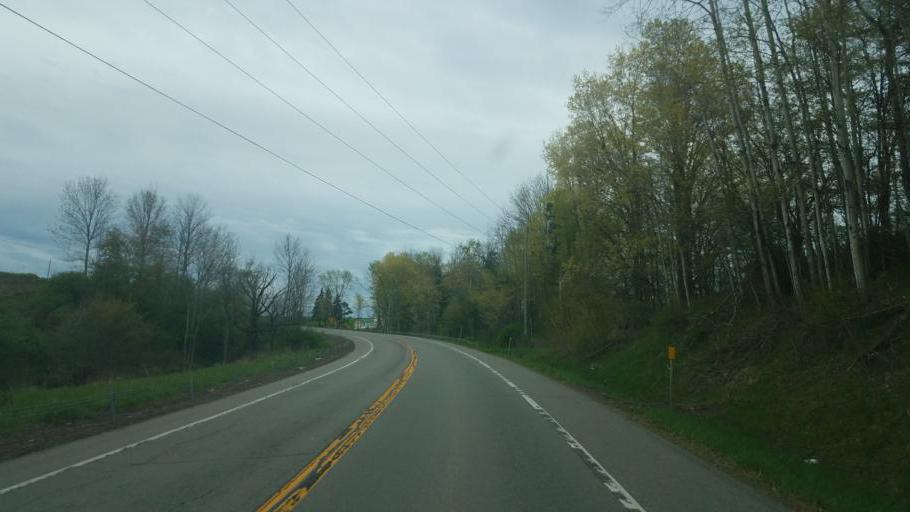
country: US
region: New York
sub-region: Steuben County
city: Canisteo
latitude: 42.1665
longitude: -77.5263
